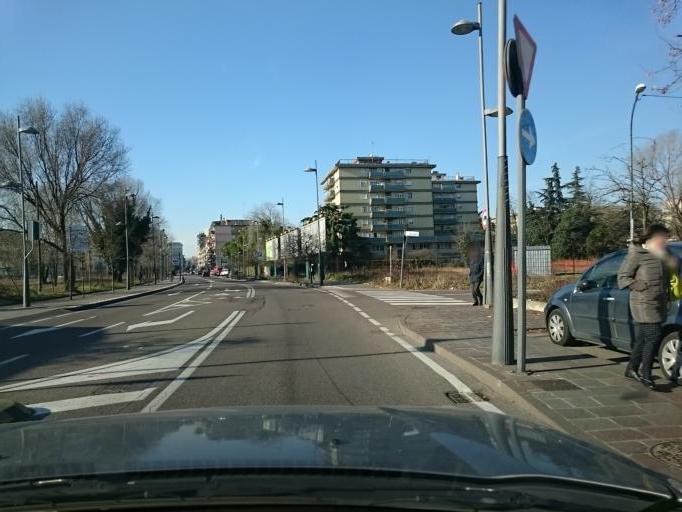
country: IT
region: Veneto
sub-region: Provincia di Venezia
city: Mestre
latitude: 45.4823
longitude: 12.2461
